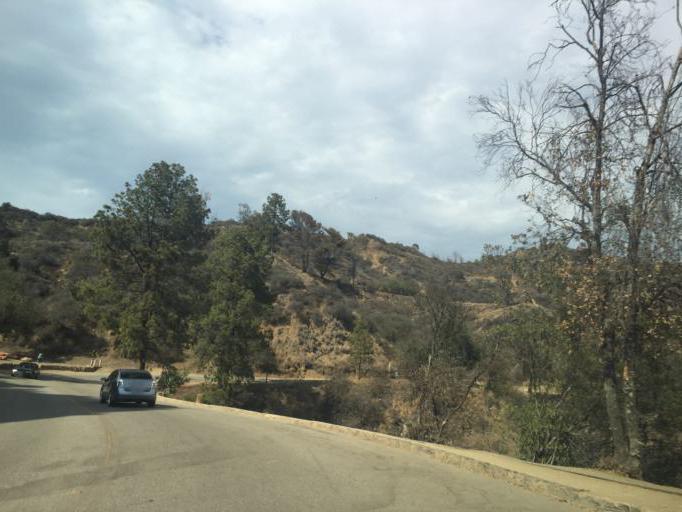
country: US
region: California
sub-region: Los Angeles County
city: Hollywood
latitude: 34.1238
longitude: -118.3063
